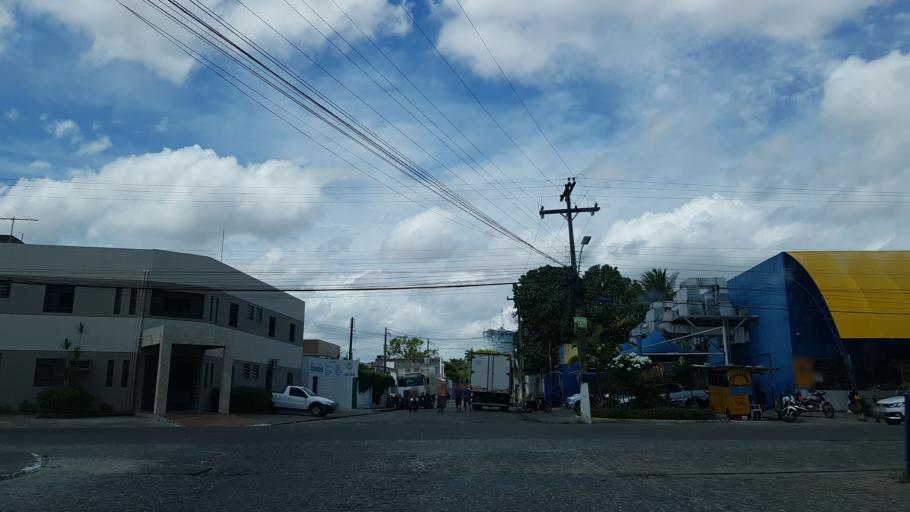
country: BR
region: Alagoas
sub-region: Penedo
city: Penedo
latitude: -10.2817
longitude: -36.5629
